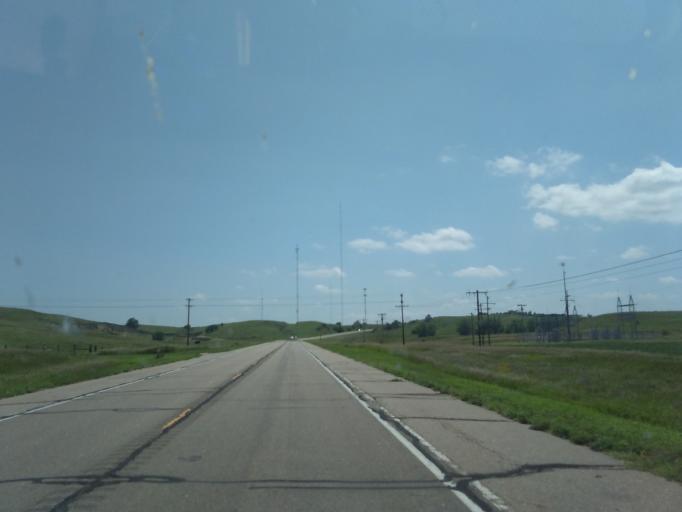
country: US
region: Nebraska
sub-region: Dawson County
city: Lexington
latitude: 40.7094
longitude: -99.7874
